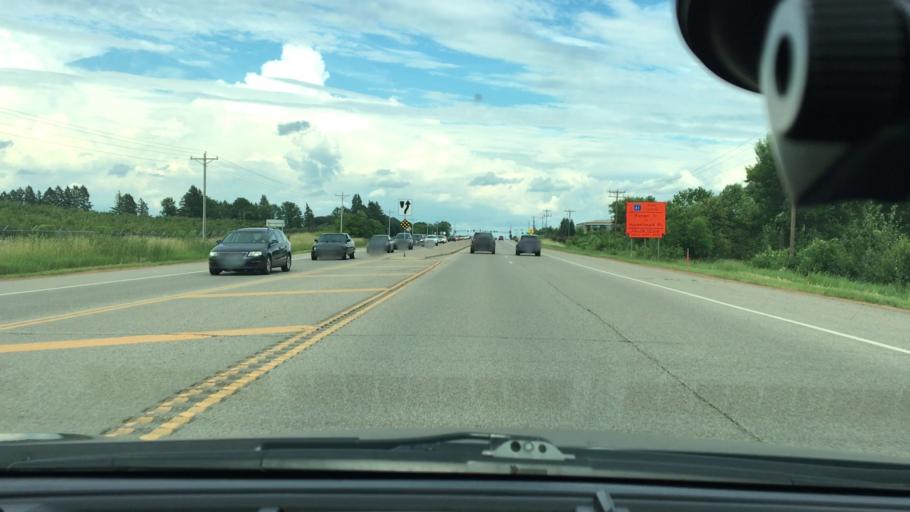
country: US
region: Minnesota
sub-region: Hennepin County
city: Shorewood
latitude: 44.8634
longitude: -93.6042
